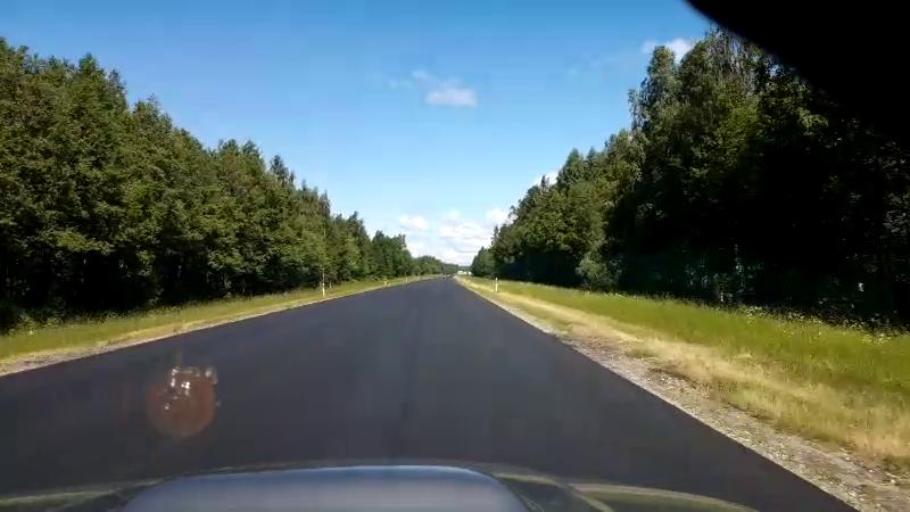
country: LV
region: Salacgrivas
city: Ainazi
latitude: 57.9653
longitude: 24.4467
